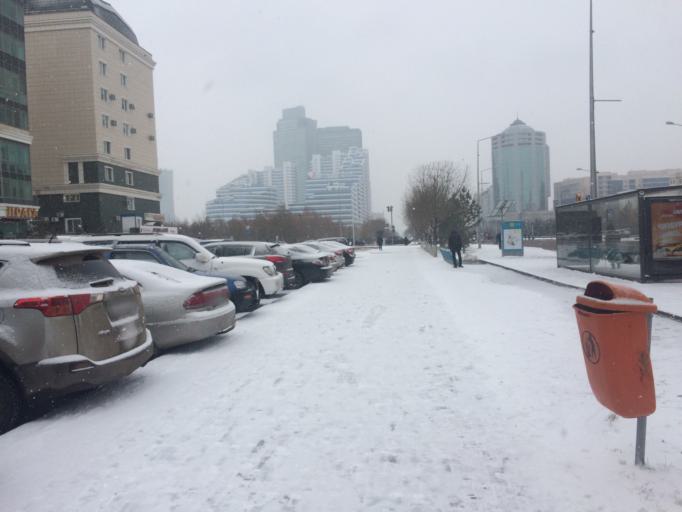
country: KZ
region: Astana Qalasy
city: Astana
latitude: 51.1299
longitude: 71.4348
